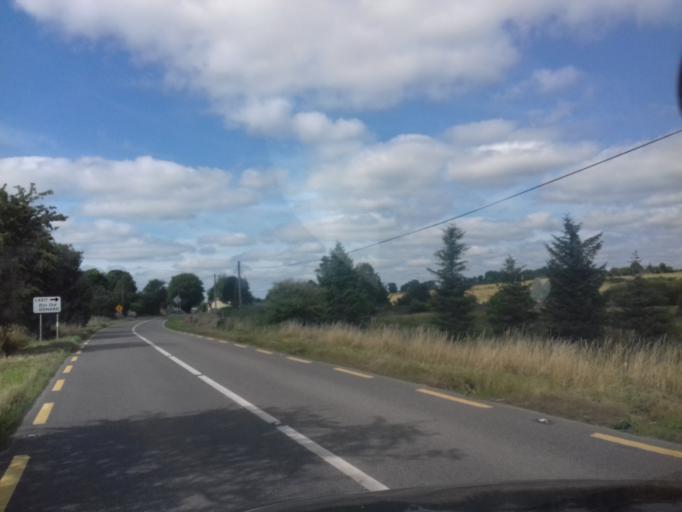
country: IE
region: Leinster
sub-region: Wicklow
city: Valleymount
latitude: 53.0353
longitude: -6.6351
